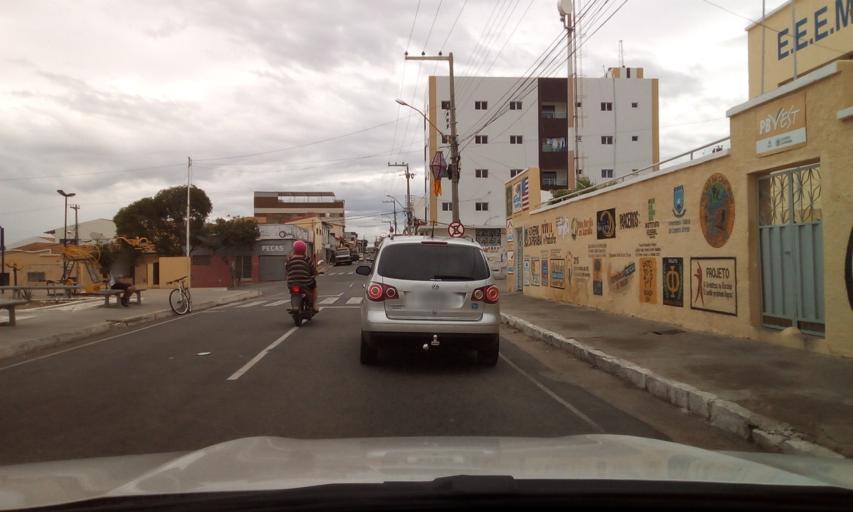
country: BR
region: Paraiba
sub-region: Picui
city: Picui
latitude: -6.5104
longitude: -36.3481
